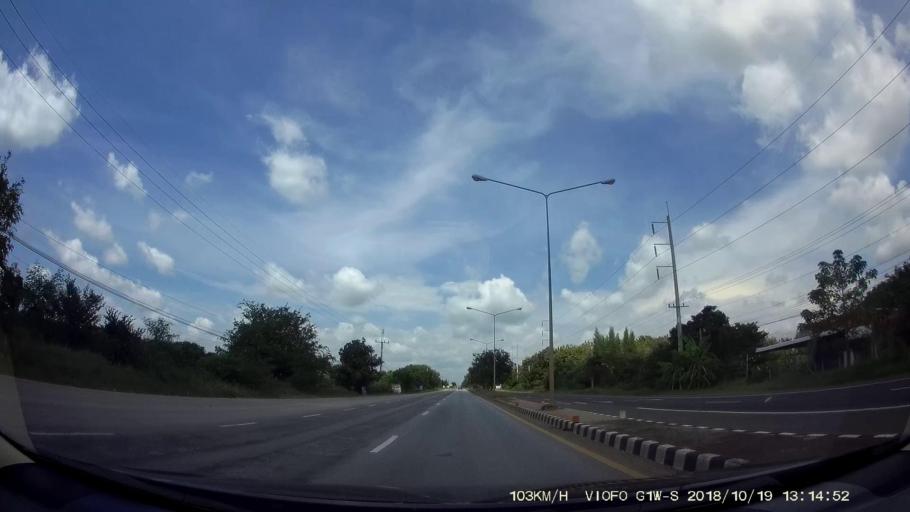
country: TH
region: Chaiyaphum
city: Chatturat
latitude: 15.3818
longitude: 101.8364
